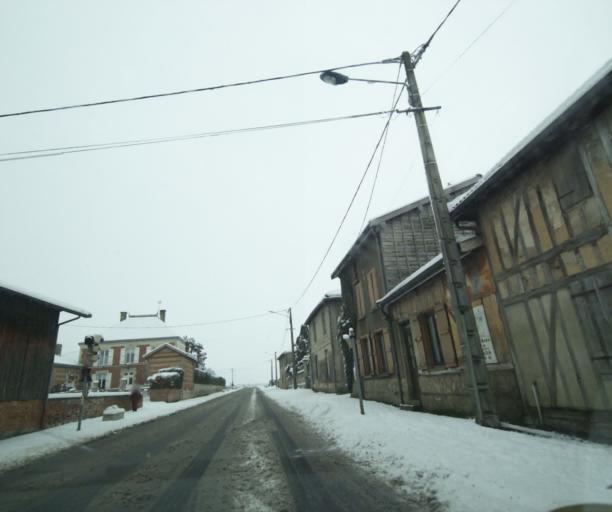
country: FR
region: Champagne-Ardenne
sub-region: Departement de la Haute-Marne
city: Saint-Dizier
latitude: 48.5823
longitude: 4.9038
